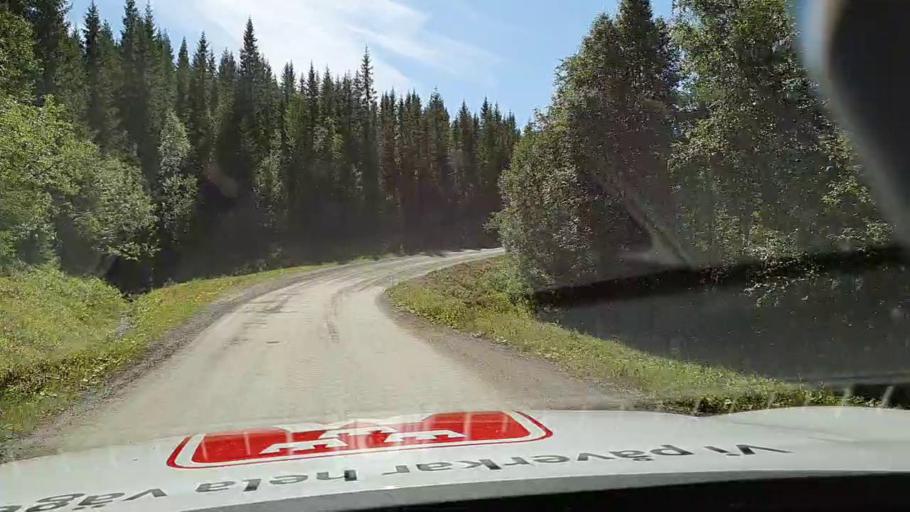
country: SE
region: Jaemtland
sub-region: Krokoms Kommun
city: Valla
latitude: 64.1024
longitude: 14.1505
